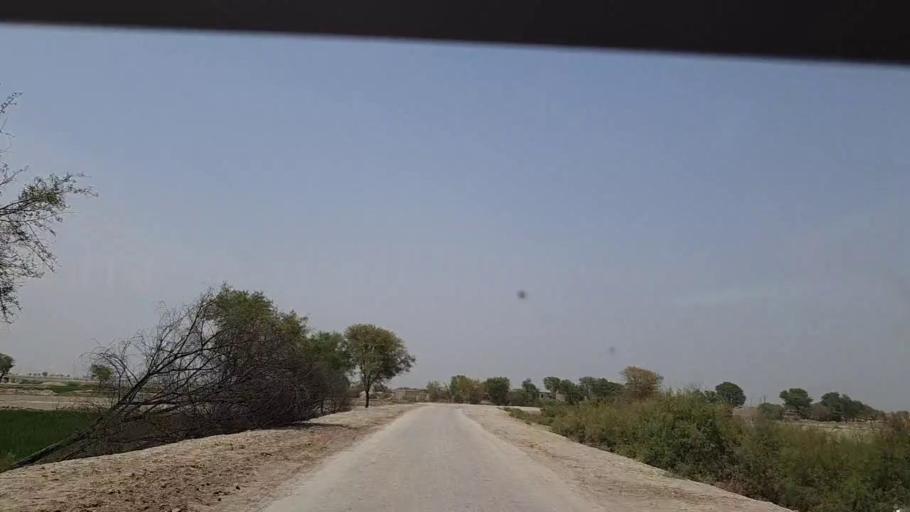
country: PK
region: Sindh
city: Khairpur Nathan Shah
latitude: 27.0513
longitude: 67.6435
